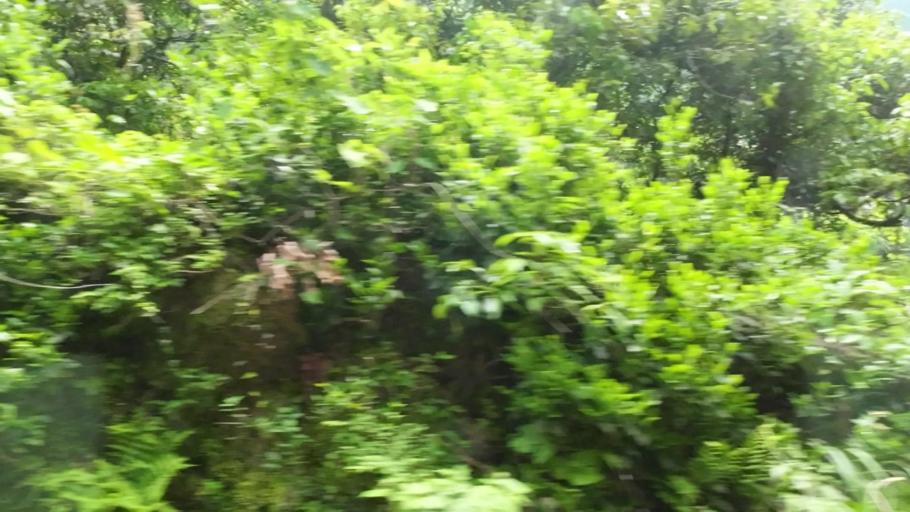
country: JP
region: Tokushima
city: Ikedacho
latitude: 33.9186
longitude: 133.7569
